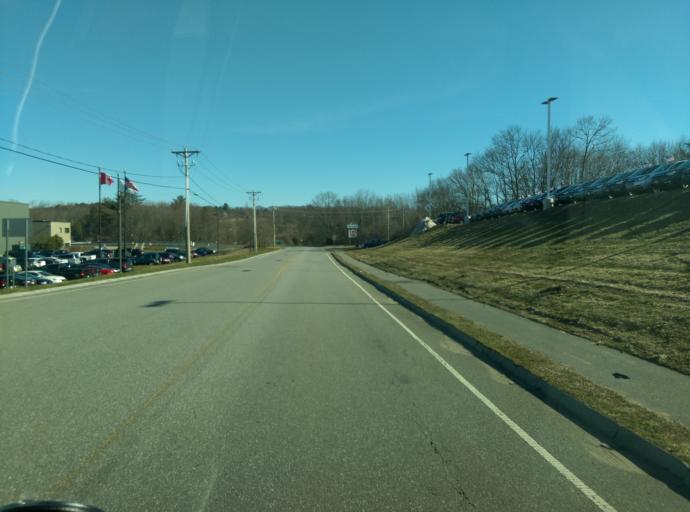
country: US
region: Massachusetts
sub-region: Essex County
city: Haverhill
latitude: 42.7852
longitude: -71.1195
